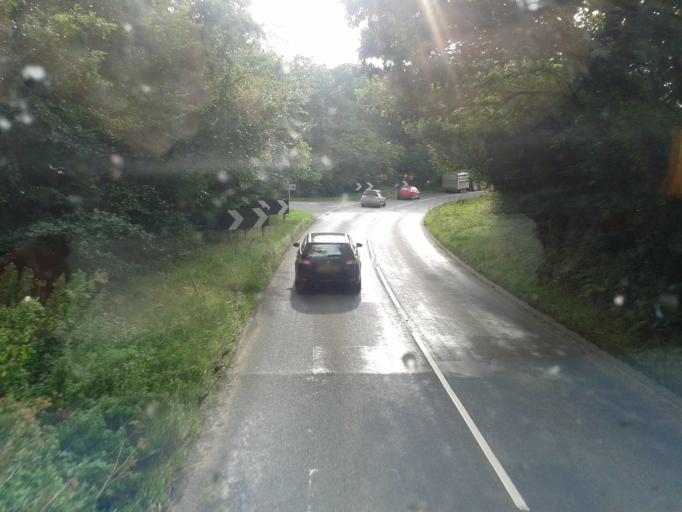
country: GB
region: England
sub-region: Devon
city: Holsworthy
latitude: 50.8131
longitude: -4.3034
